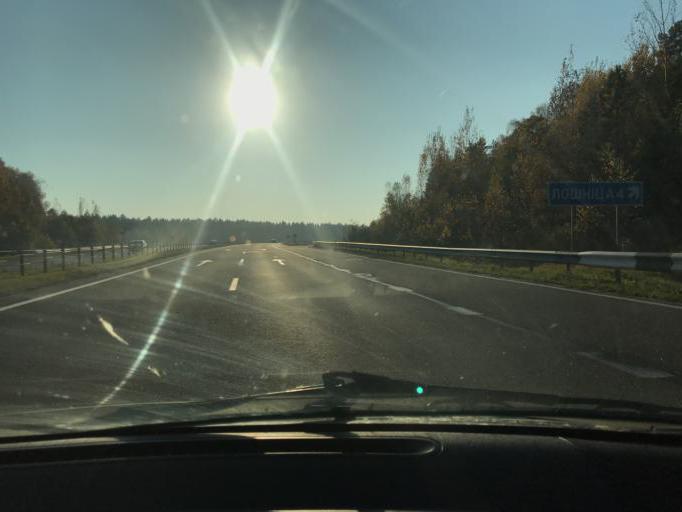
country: BY
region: Minsk
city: Loshnitsa
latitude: 54.2737
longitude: 28.7205
